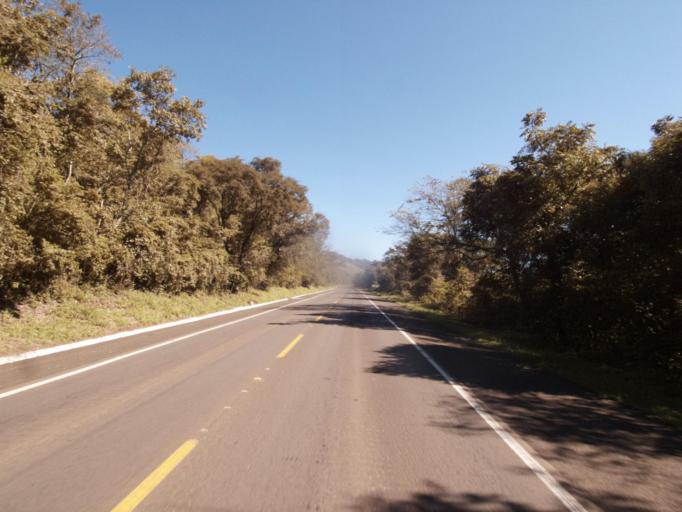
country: BR
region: Rio Grande do Sul
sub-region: Frederico Westphalen
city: Frederico Westphalen
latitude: -26.8236
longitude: -53.3921
